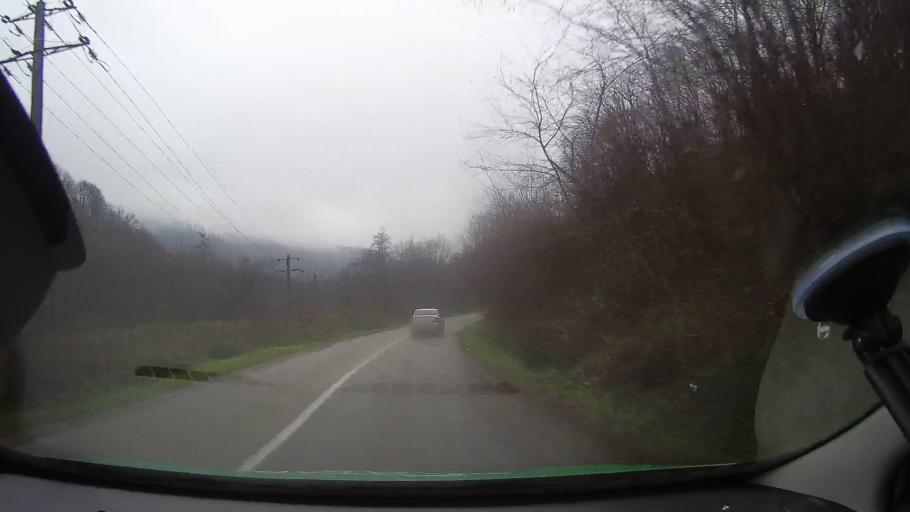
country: RO
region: Arad
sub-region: Comuna Dezna
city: Dezna
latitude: 46.4120
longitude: 22.2560
